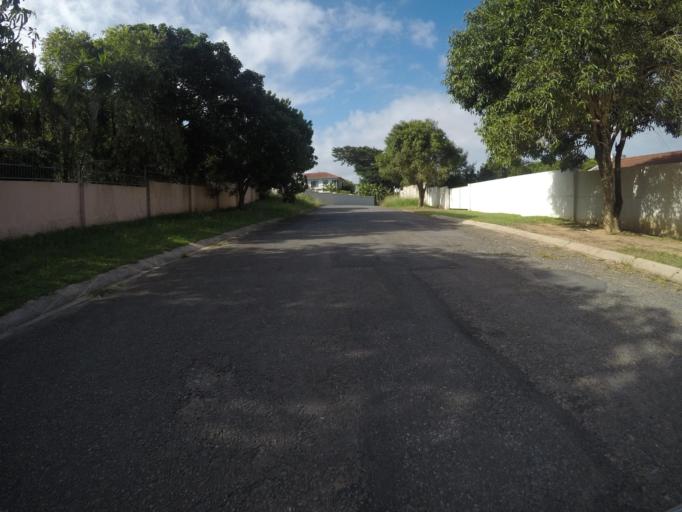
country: ZA
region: Eastern Cape
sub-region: Buffalo City Metropolitan Municipality
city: East London
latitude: -32.9710
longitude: 27.9565
